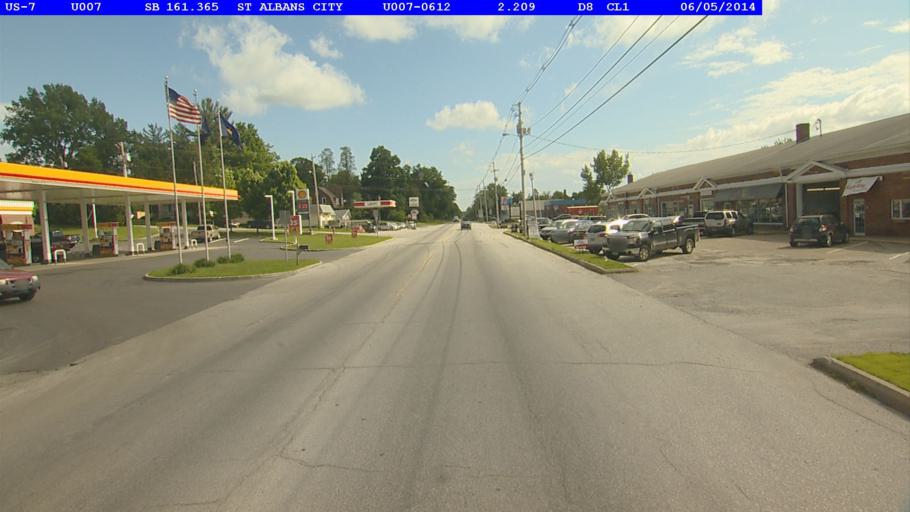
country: US
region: Vermont
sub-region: Franklin County
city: Saint Albans
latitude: 44.8245
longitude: -73.0809
